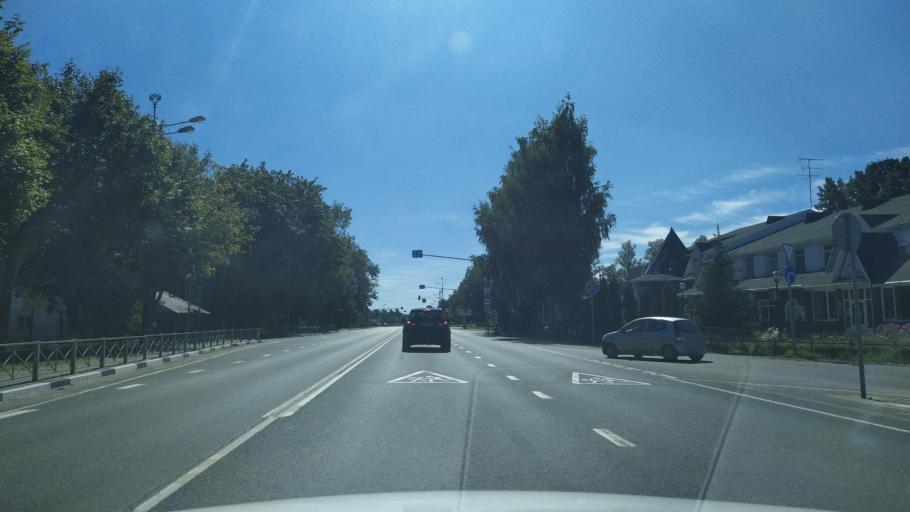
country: RU
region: Pskov
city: Pskov
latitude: 57.7965
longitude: 28.4182
